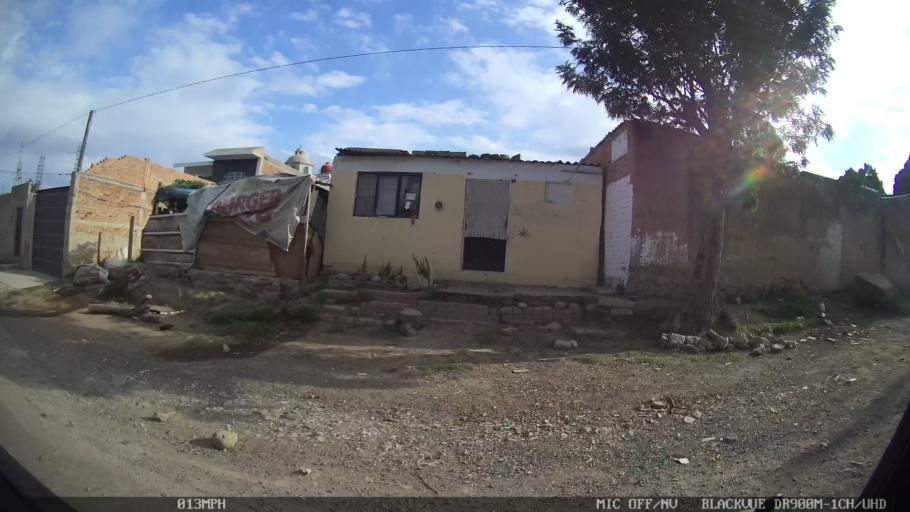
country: MX
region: Jalisco
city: Tonala
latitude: 20.6728
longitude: -103.2444
